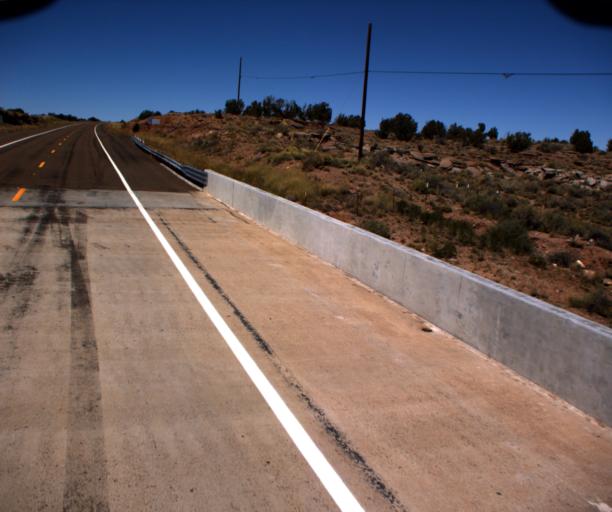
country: US
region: Arizona
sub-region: Apache County
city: Saint Johns
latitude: 34.6484
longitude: -109.7032
